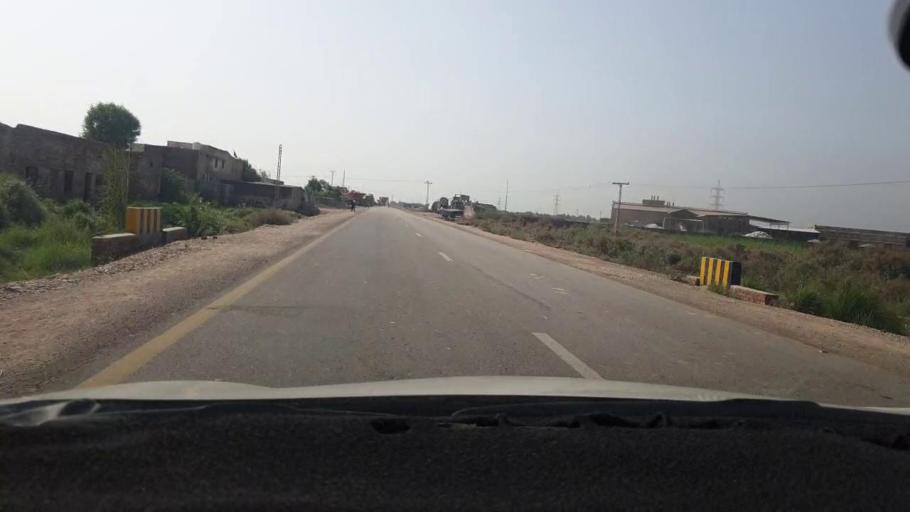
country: PK
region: Sindh
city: Sanghar
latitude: 25.9734
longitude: 68.9706
